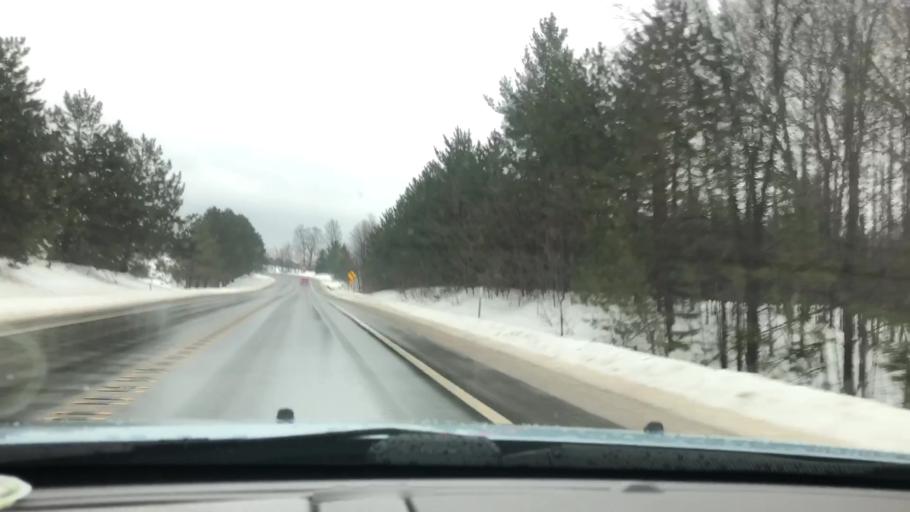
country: US
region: Michigan
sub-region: Charlevoix County
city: East Jordan
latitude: 45.0985
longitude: -85.0261
